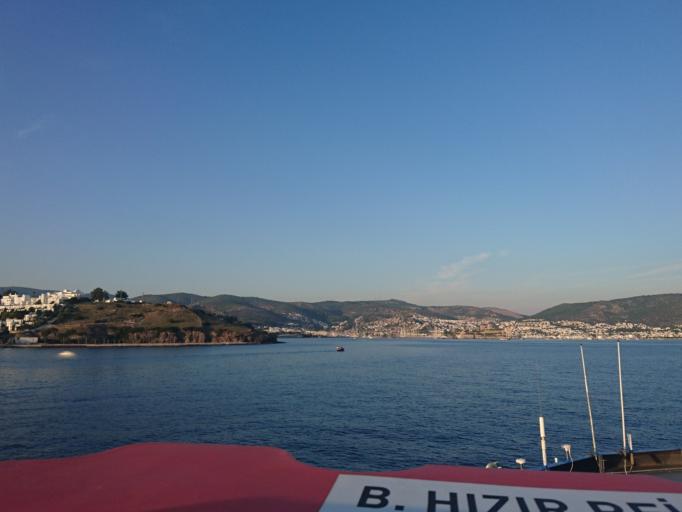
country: TR
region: Mugla
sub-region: Bodrum
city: Bodrum
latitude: 37.0170
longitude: 27.4181
